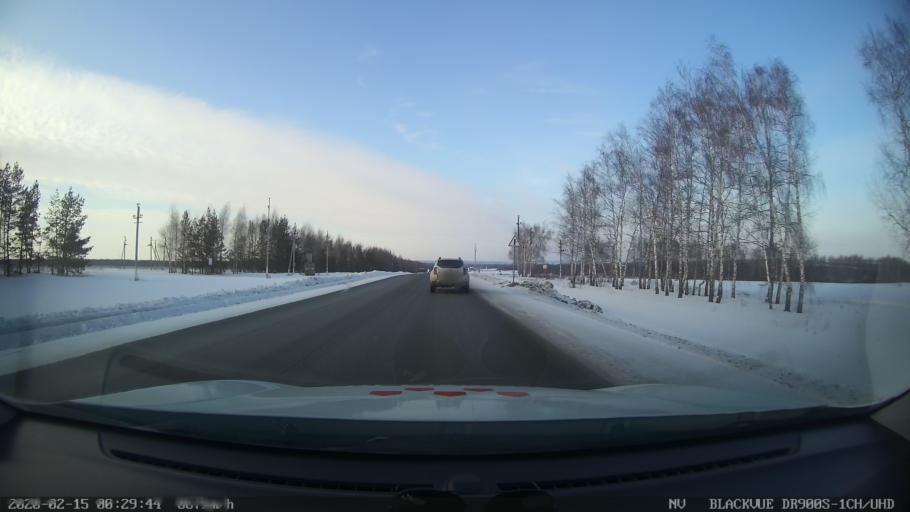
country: RU
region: Tatarstan
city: Verkhniy Uslon
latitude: 55.6535
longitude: 48.8649
